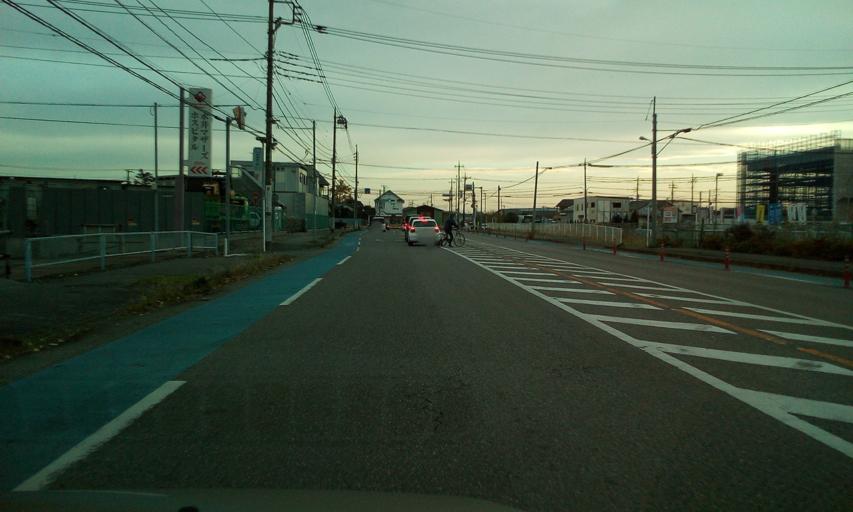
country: JP
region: Saitama
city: Yashio-shi
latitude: 35.8506
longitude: 139.8603
